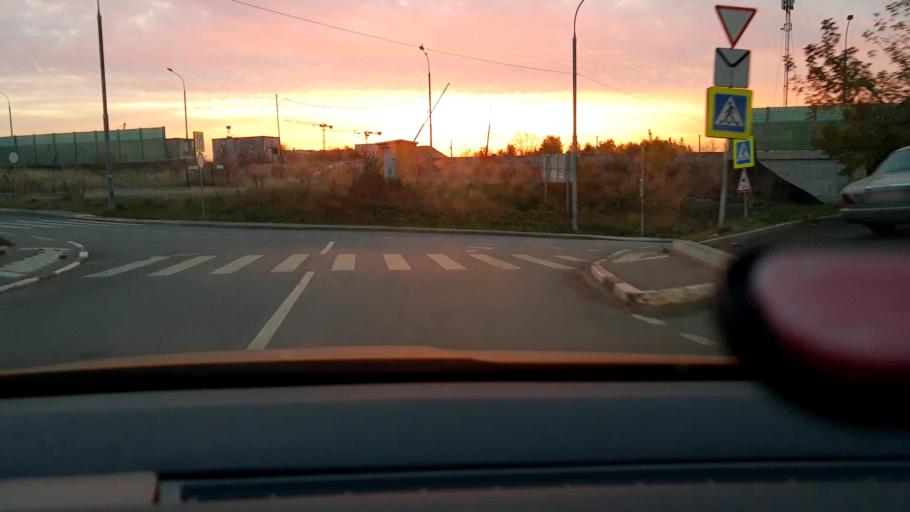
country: RU
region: Moskovskaya
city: Marfino
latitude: 55.7010
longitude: 37.3836
